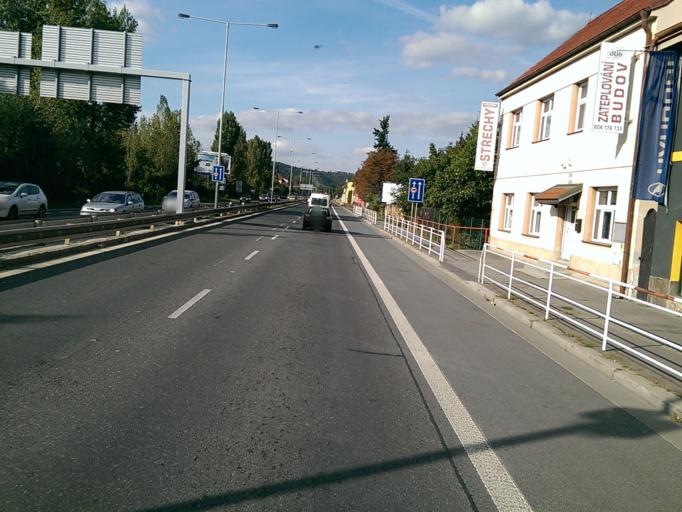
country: CZ
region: Praha
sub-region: Praha 12
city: Modrany
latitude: 49.9973
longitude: 14.3967
